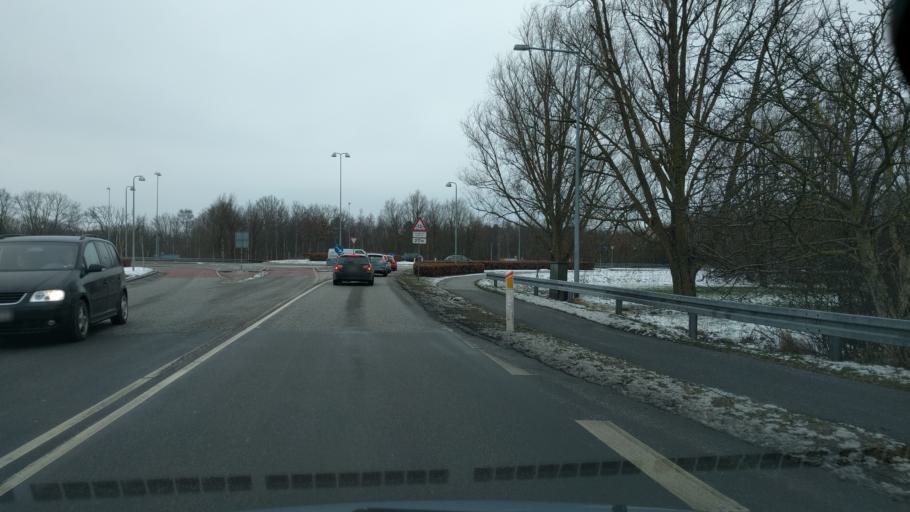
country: DK
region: Zealand
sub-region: Guldborgsund Kommune
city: Nykobing Falster
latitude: 54.7582
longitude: 11.8556
